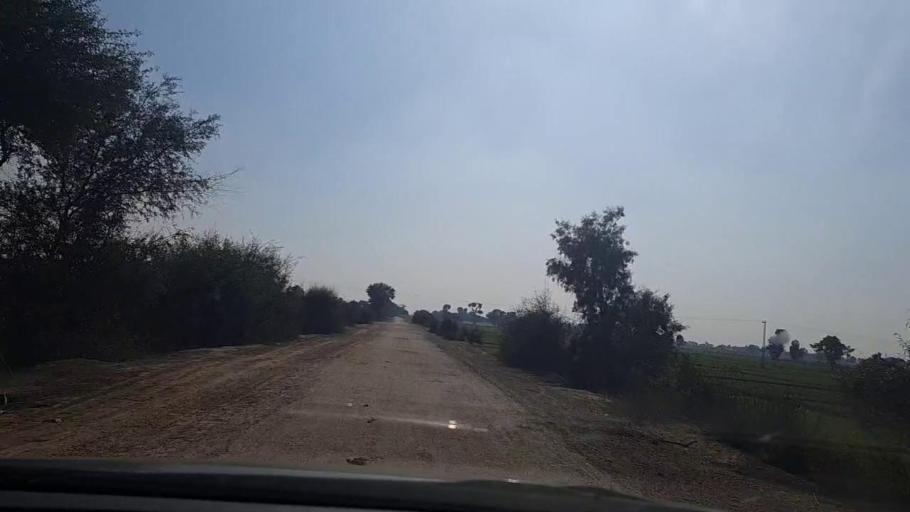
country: PK
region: Sindh
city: Daulatpur
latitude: 26.2889
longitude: 68.0678
